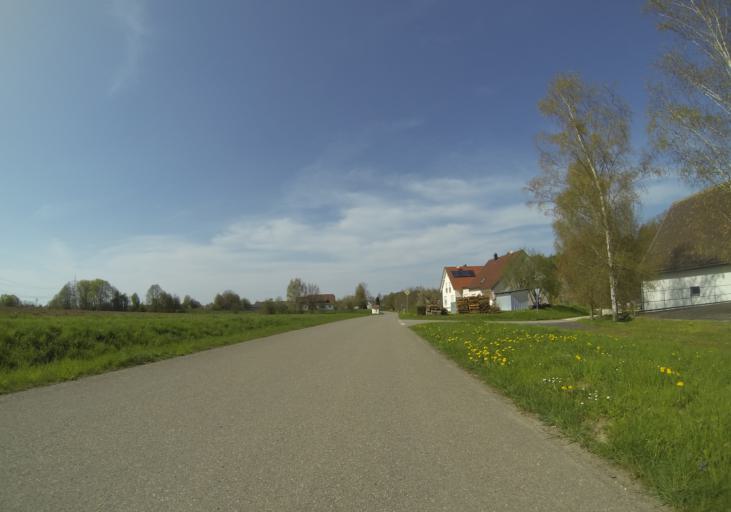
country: DE
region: Baden-Wuerttemberg
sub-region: Tuebingen Region
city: Huttisheim
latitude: 48.2723
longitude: 9.9473
